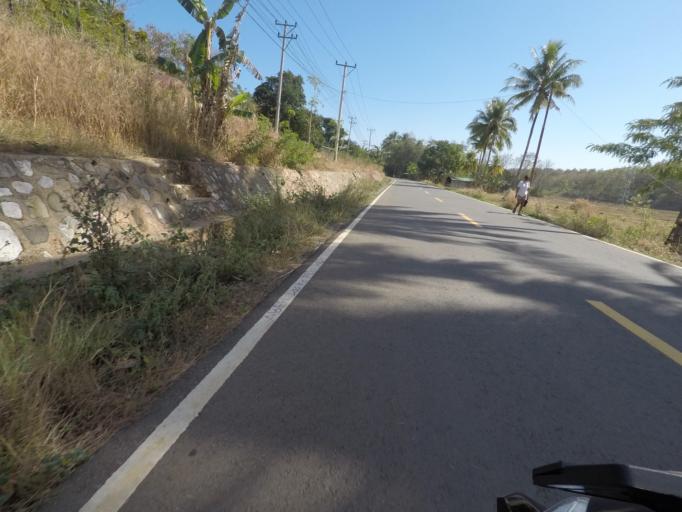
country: TL
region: Bobonaro
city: Maliana
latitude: -8.9552
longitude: 125.2123
